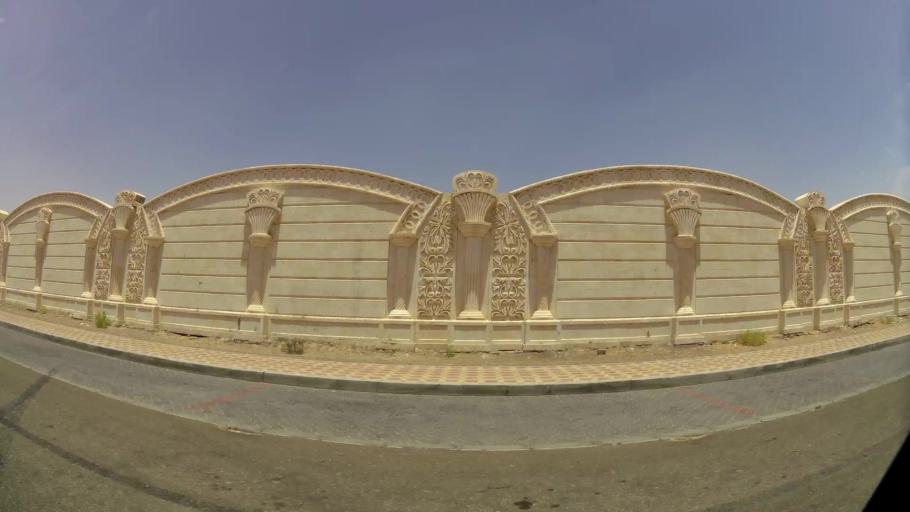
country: OM
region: Al Buraimi
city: Al Buraymi
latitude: 24.2704
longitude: 55.7150
